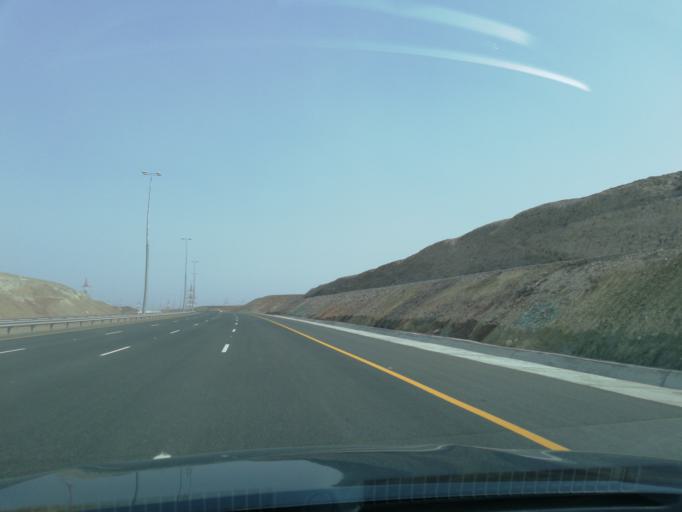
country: OM
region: Al Batinah
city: Al Liwa'
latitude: 24.3410
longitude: 56.5514
